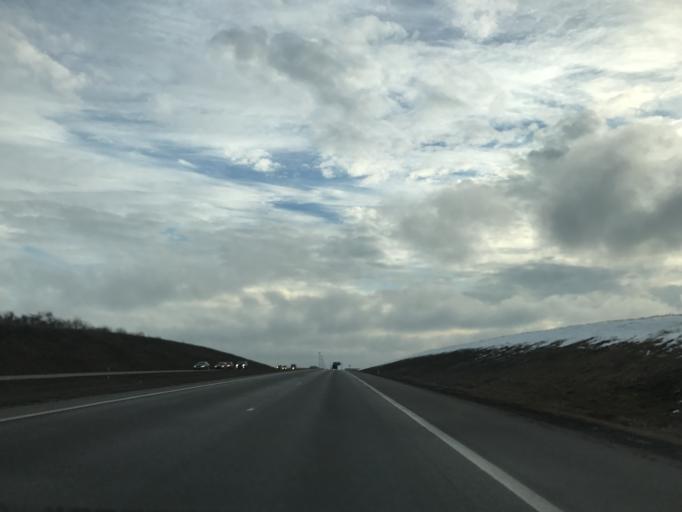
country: RU
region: Rostov
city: Glubokiy
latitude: 48.4658
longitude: 40.3407
